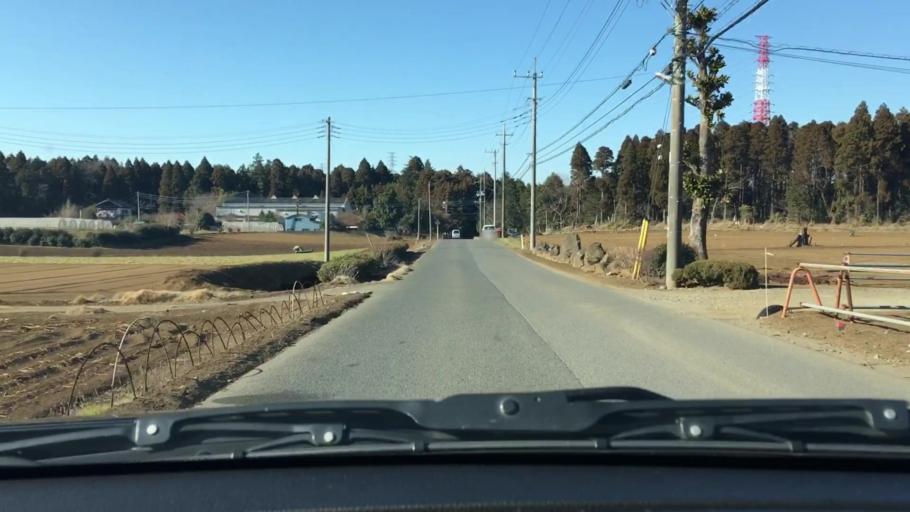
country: JP
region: Chiba
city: Shisui
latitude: 35.6983
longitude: 140.2906
